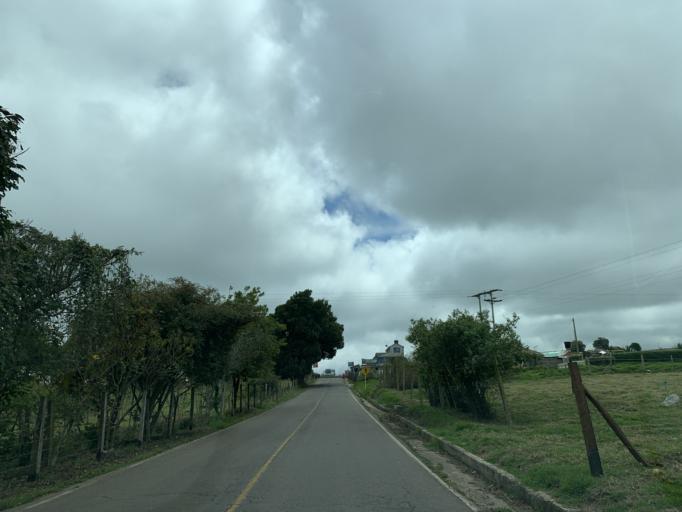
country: CO
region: Boyaca
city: Tunja
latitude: 5.5822
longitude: -73.3515
